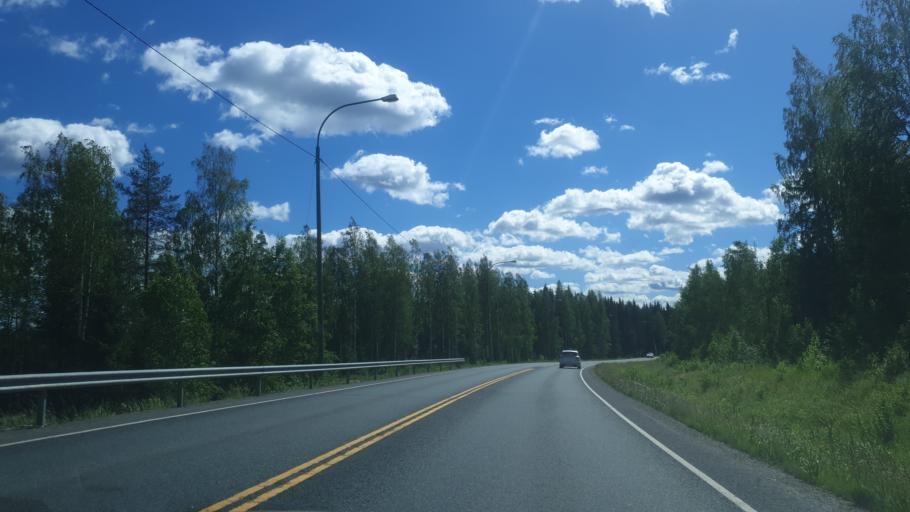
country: FI
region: Northern Savo
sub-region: Varkaus
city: Leppaevirta
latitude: 62.5661
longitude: 27.6174
